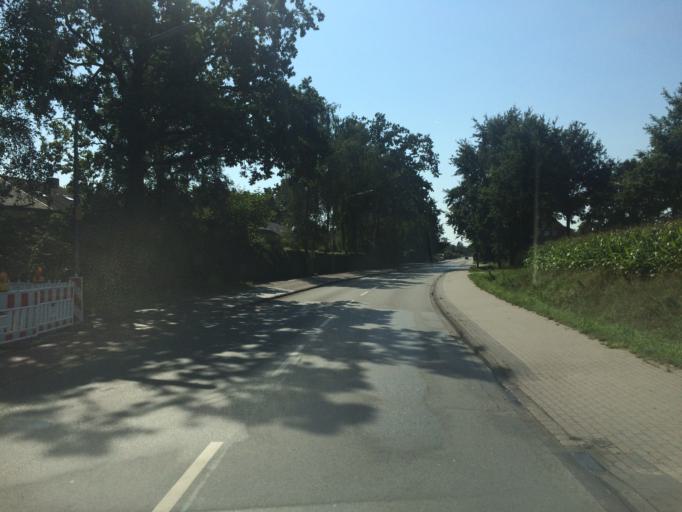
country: DE
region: North Rhine-Westphalia
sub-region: Regierungsbezirk Munster
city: Telgte
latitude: 52.0039
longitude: 7.7099
